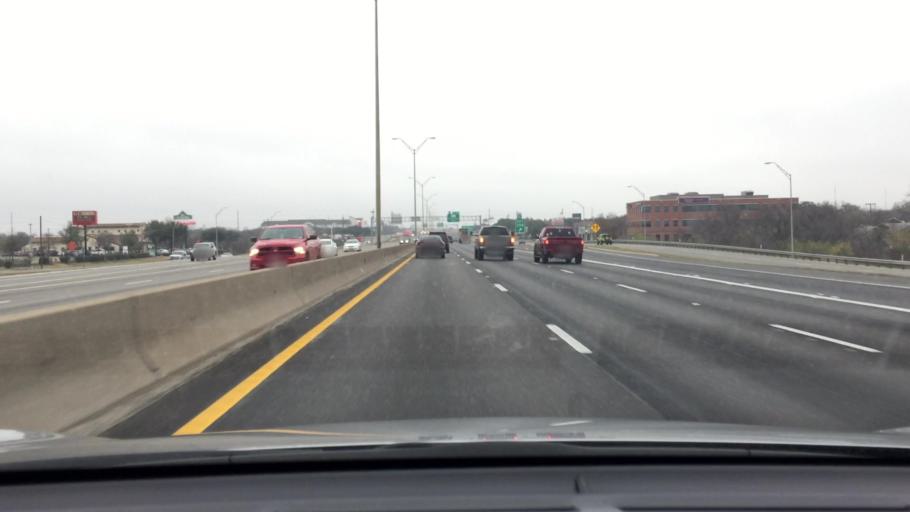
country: US
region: Texas
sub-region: Williamson County
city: Round Rock
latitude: 30.5207
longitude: -97.6891
